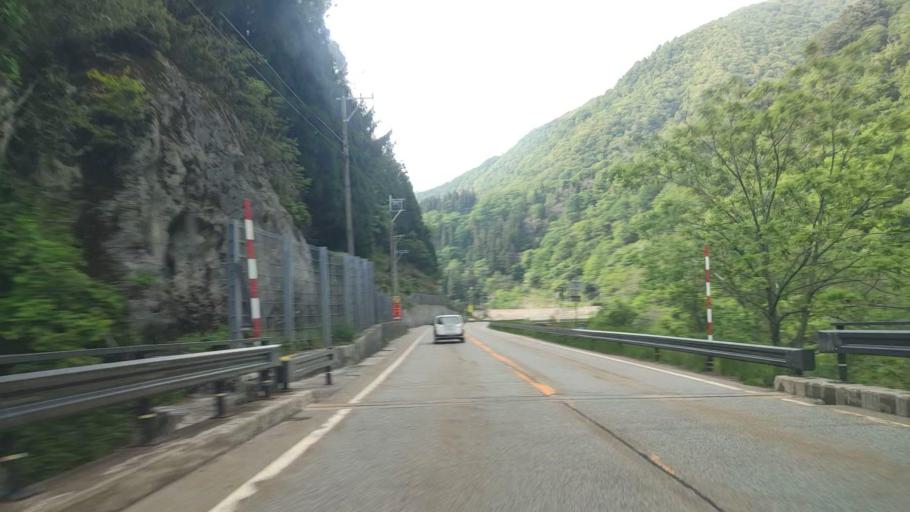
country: JP
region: Gifu
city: Takayama
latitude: 36.3580
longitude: 137.2884
